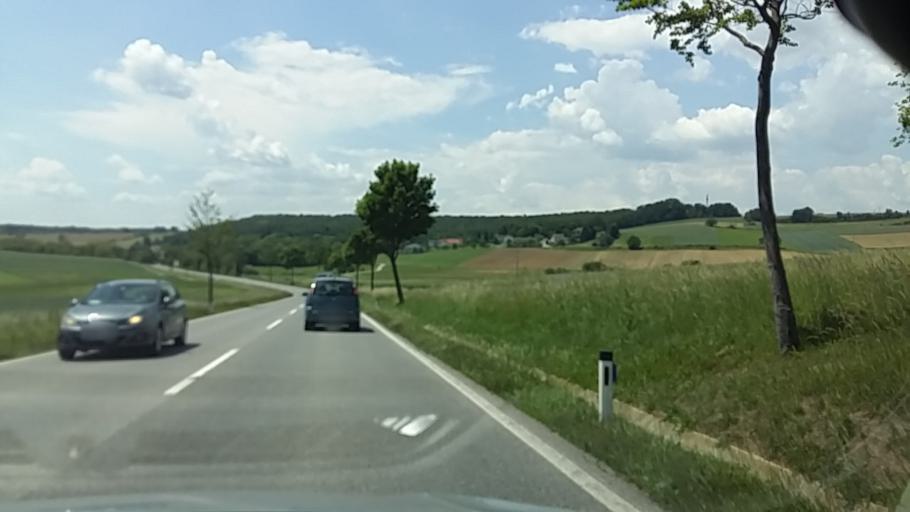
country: AT
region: Burgenland
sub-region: Politischer Bezirk Oberwart
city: Mariasdorf
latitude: 47.3533
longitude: 16.2315
